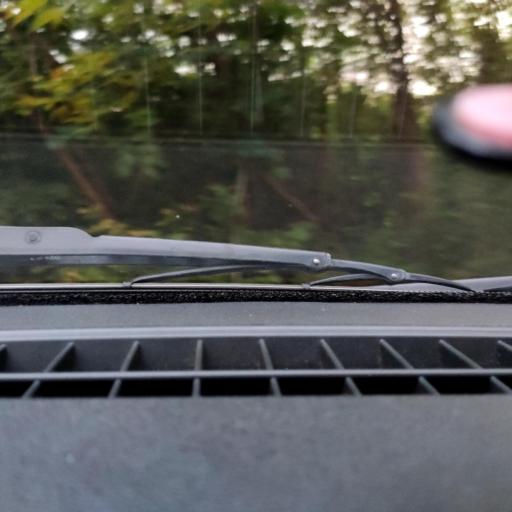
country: RU
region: Bashkortostan
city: Ufa
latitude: 54.7766
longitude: 56.0167
